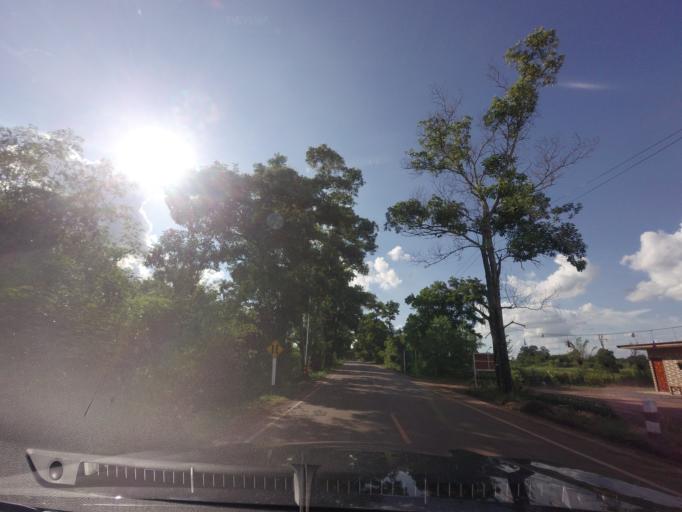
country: TH
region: Changwat Udon Thani
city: Ban Dung
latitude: 17.7417
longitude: 103.3420
